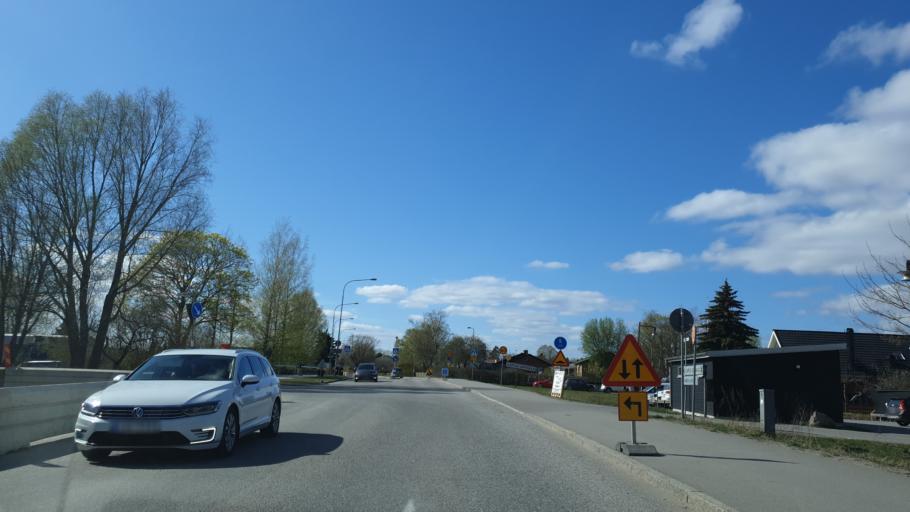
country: SE
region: Uppsala
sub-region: Uppsala Kommun
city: Gamla Uppsala
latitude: 59.8917
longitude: 17.6498
